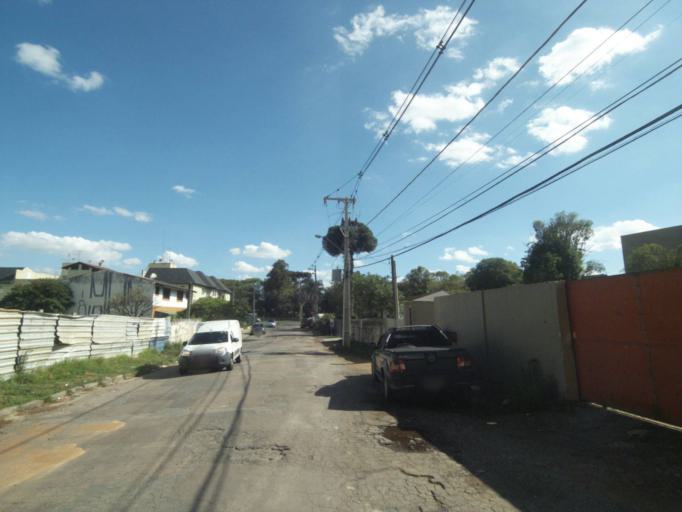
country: BR
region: Parana
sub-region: Curitiba
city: Curitiba
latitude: -25.4432
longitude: -49.3430
